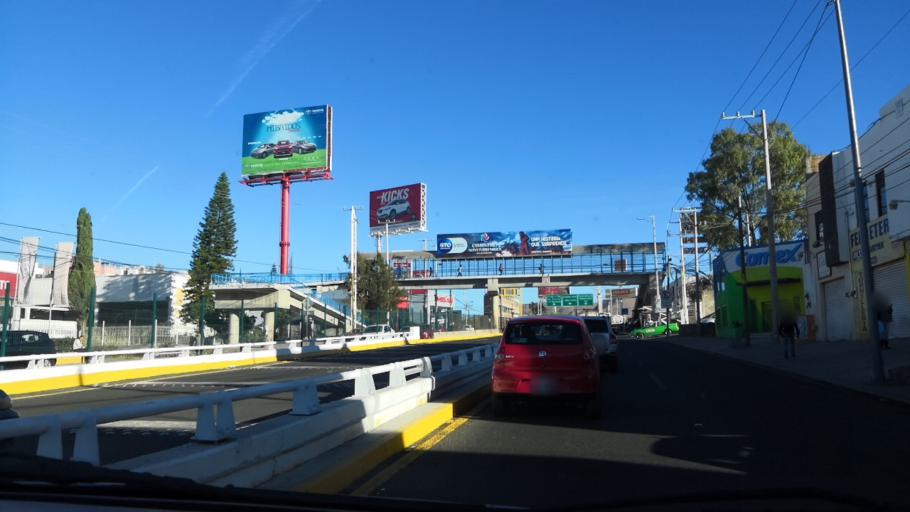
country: MX
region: Guanajuato
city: Marfil
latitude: 20.9889
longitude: -101.2850
